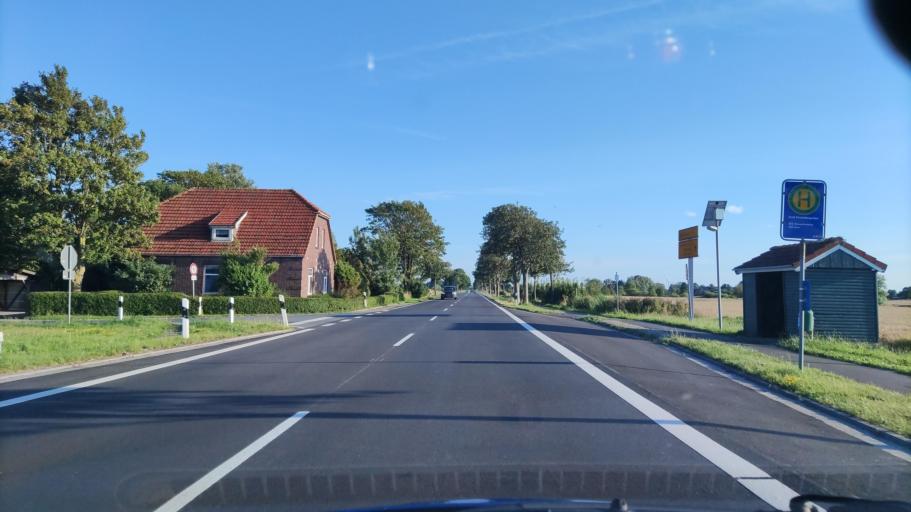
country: DE
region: Lower Saxony
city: Werdum
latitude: 53.6754
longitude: 7.7930
